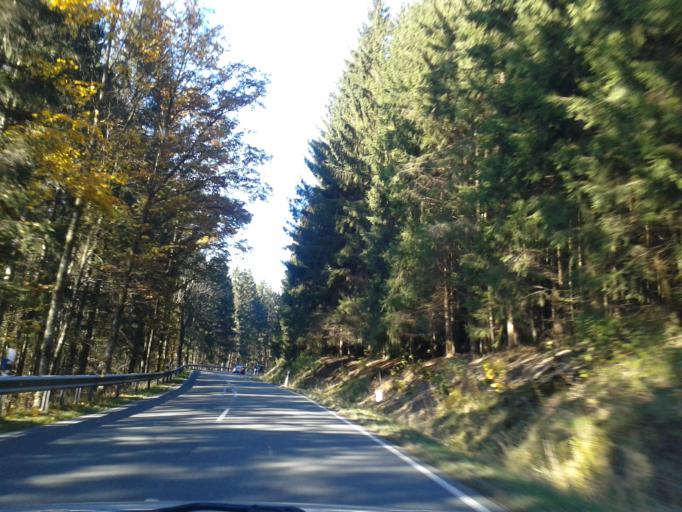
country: DE
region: North Rhine-Westphalia
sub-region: Regierungsbezirk Arnsberg
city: Bad Berleburg
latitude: 51.0980
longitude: 8.4333
